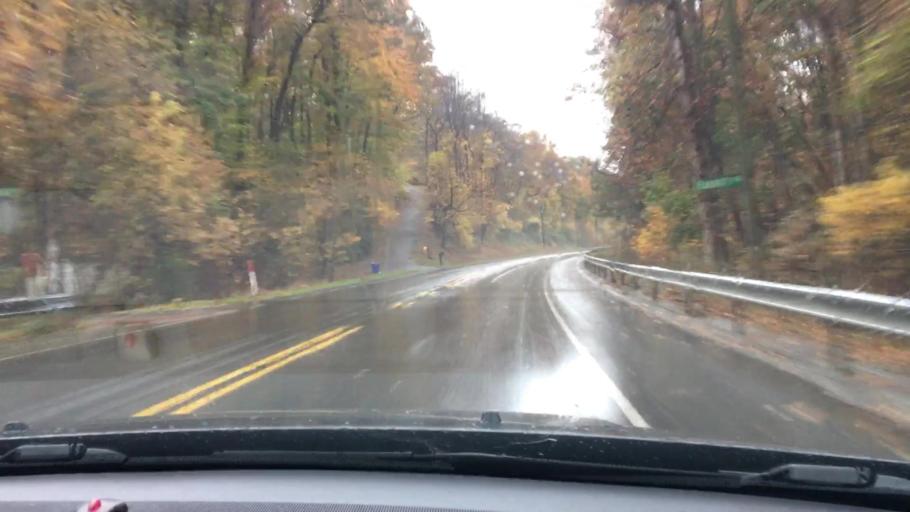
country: US
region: Pennsylvania
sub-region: York County
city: Susquehanna Trails
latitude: 39.8086
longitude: -76.3360
